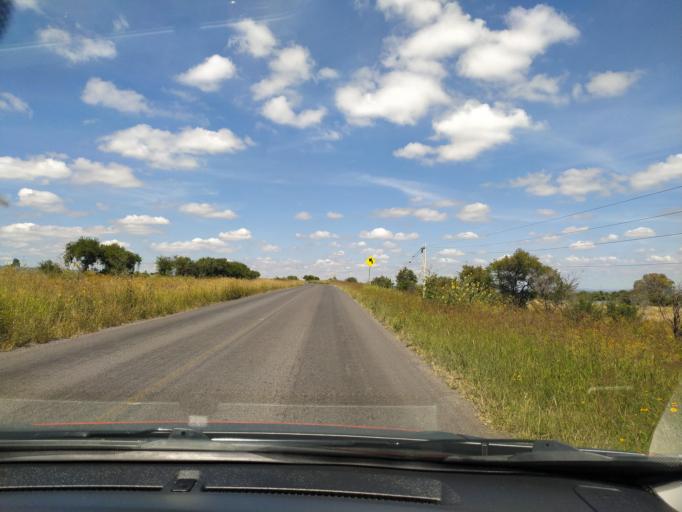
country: MX
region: Jalisco
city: San Diego de Alejandria
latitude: 21.0062
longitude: -102.0105
